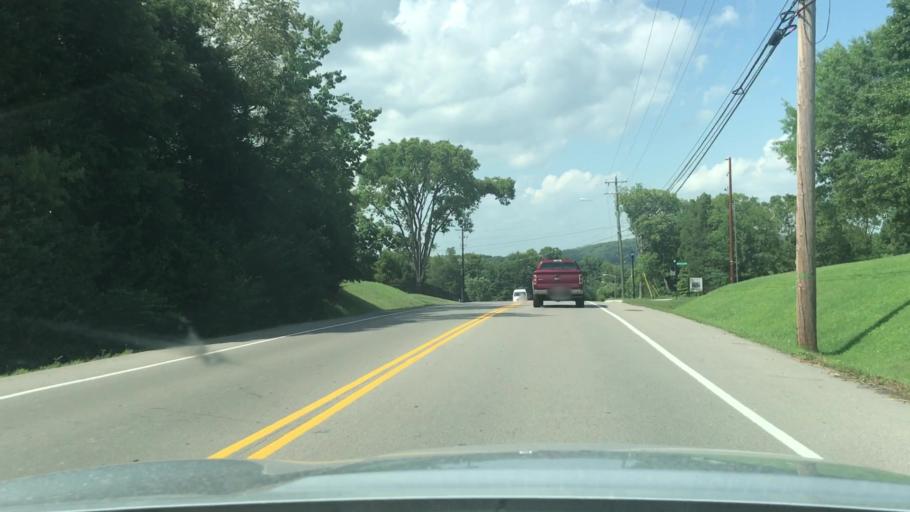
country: US
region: Tennessee
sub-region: Williamson County
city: Brentwood Estates
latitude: 36.0073
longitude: -86.7425
